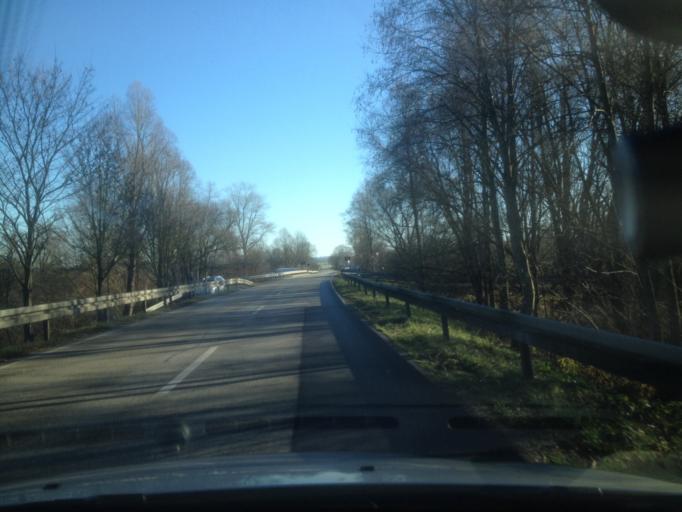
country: DE
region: Bavaria
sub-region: Upper Bavaria
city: Berglern
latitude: 48.4110
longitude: 11.9097
